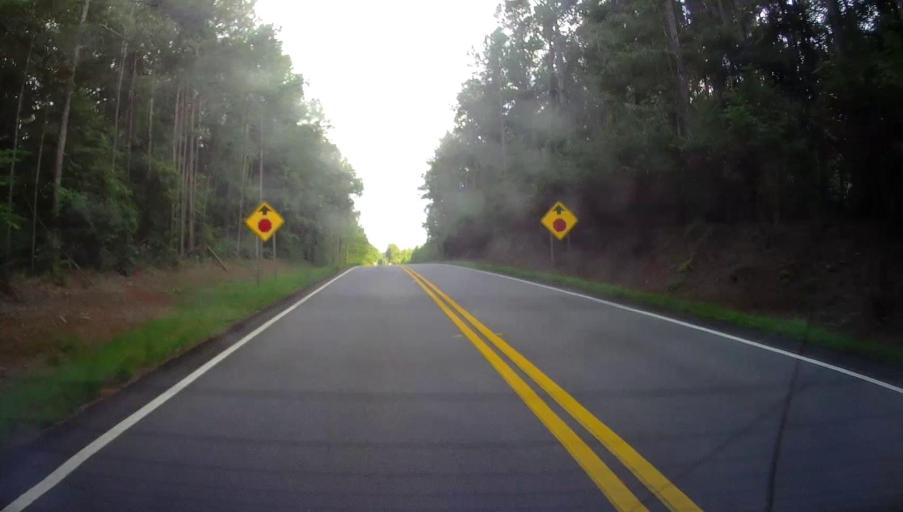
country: US
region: Georgia
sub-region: Crawford County
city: Knoxville
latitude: 32.8801
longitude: -83.9957
